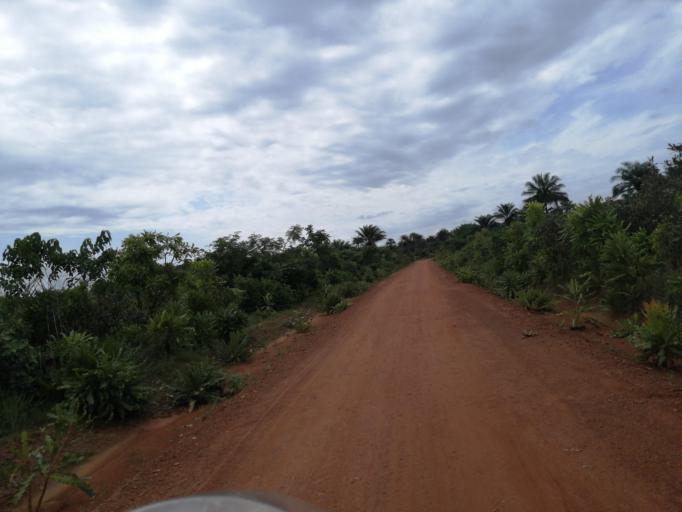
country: SL
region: Northern Province
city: Port Loko
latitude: 8.7691
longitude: -12.9091
